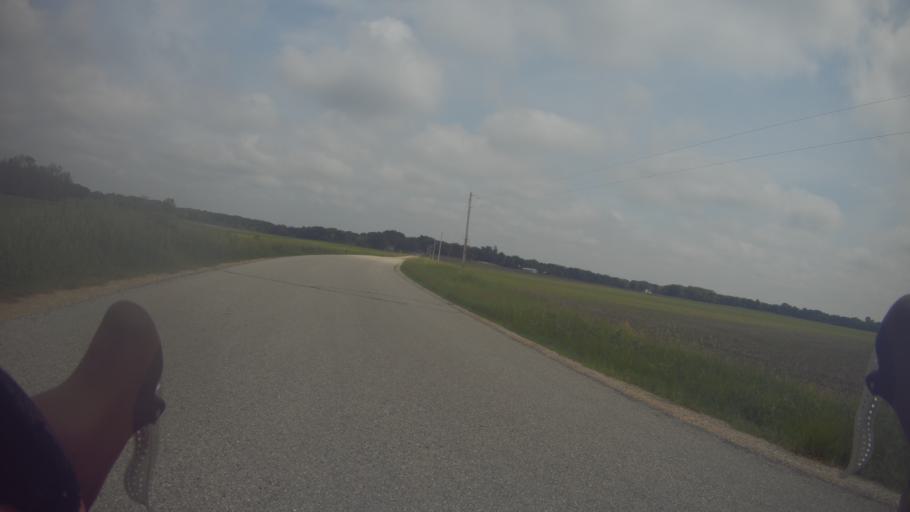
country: US
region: Wisconsin
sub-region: Jefferson County
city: Cambridge
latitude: 42.9242
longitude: -89.0037
